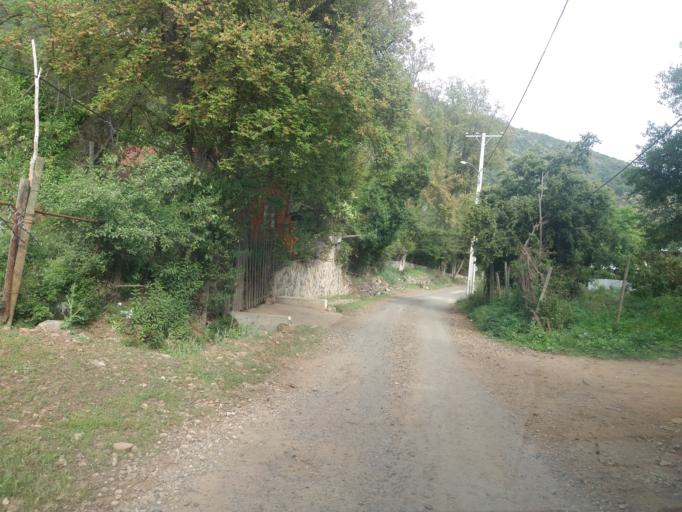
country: CL
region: Valparaiso
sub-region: Provincia de Marga Marga
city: Limache
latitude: -33.0710
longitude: -71.0617
